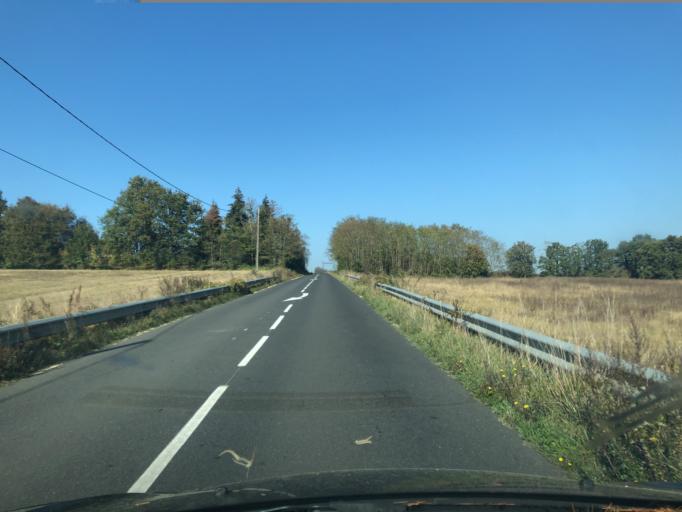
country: FR
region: Centre
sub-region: Departement d'Indre-et-Loire
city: Cerelles
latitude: 47.4863
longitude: 0.6616
